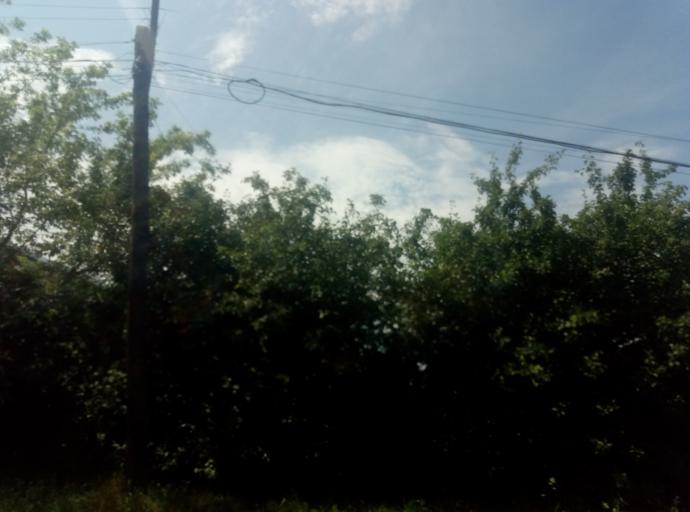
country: RU
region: Tula
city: Dubovka
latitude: 53.9029
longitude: 38.0312
